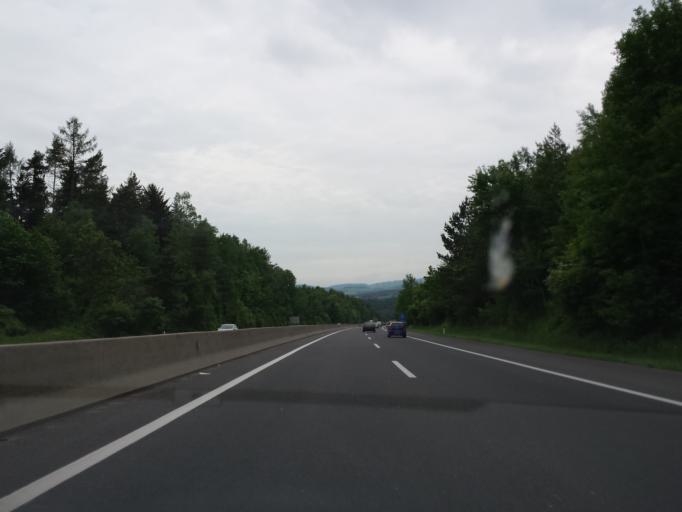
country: AT
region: Lower Austria
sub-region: Politischer Bezirk Neunkirchen
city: Seebenstein
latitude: 47.6918
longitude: 16.1286
